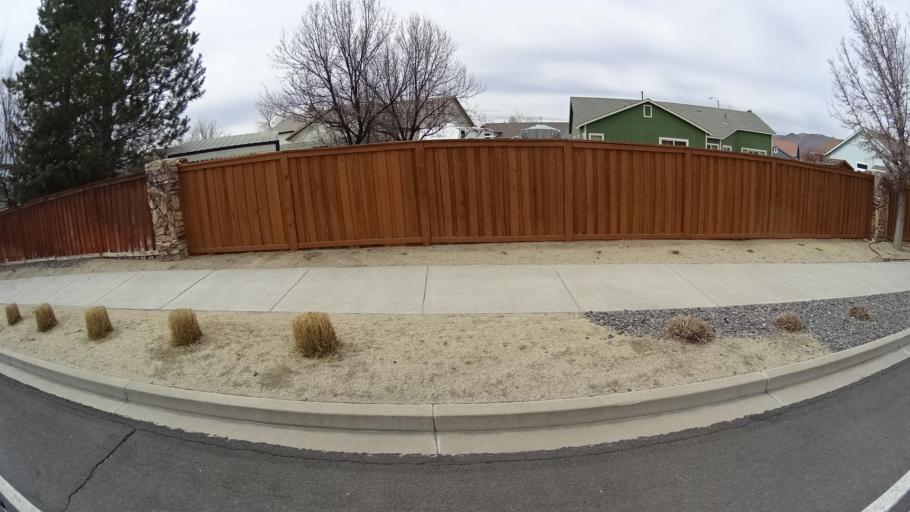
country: US
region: Nevada
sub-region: Washoe County
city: Spanish Springs
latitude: 39.6301
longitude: -119.6902
